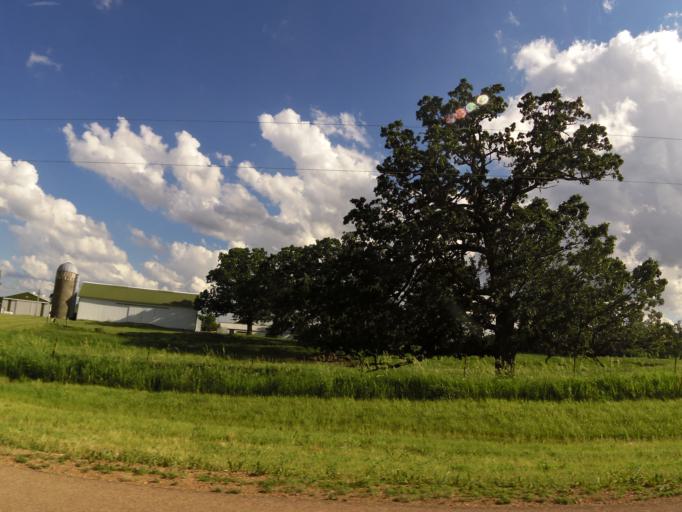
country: US
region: Minnesota
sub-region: Carver County
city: Victoria
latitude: 44.8117
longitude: -93.6709
